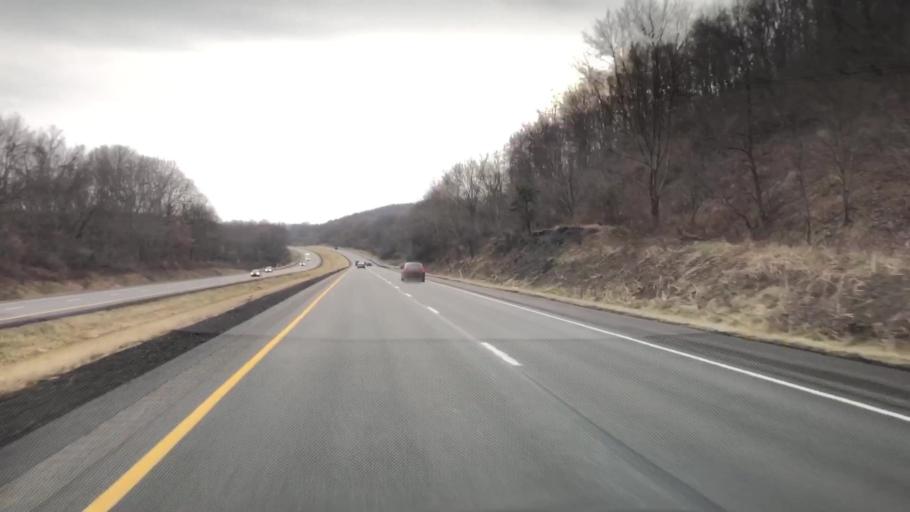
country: US
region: Pennsylvania
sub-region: Butler County
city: Prospect
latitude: 40.8648
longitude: -80.1099
